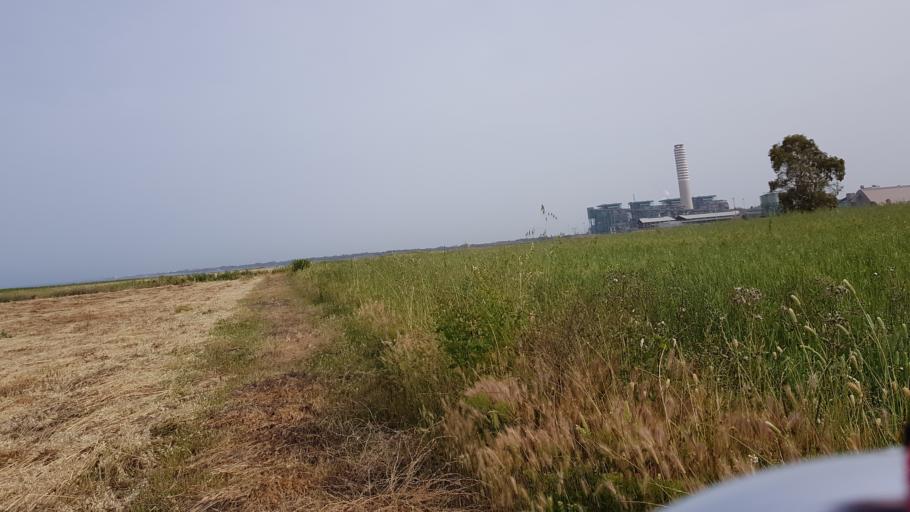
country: IT
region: Apulia
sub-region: Provincia di Brindisi
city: La Rosa
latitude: 40.5797
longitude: 18.0351
